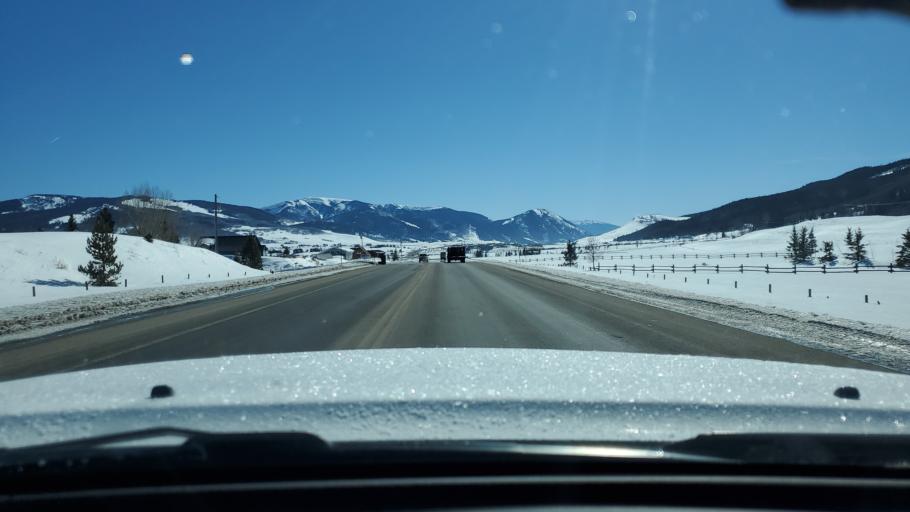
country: US
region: Colorado
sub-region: Gunnison County
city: Crested Butte
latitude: 38.8594
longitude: -106.9691
